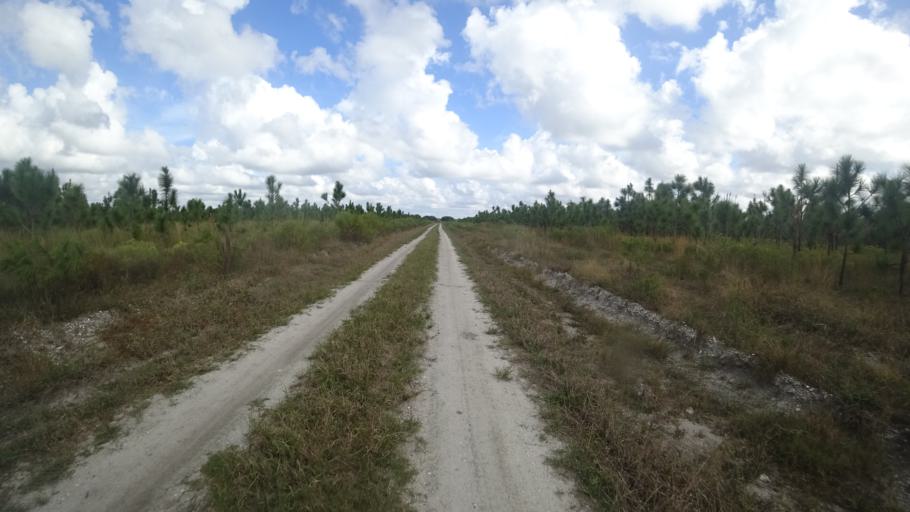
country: US
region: Florida
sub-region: Hillsborough County
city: Wimauma
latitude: 27.5047
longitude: -82.1442
